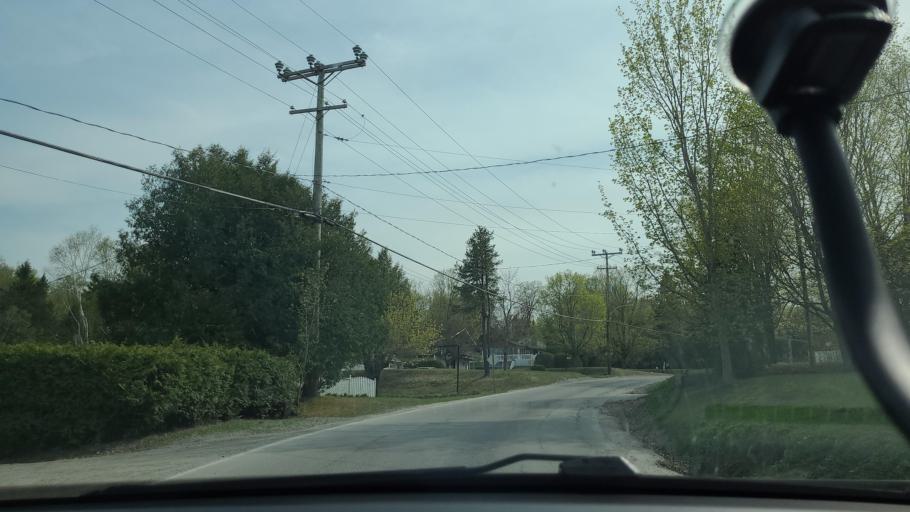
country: CA
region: Quebec
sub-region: Laurentides
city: Prevost
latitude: 45.8935
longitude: -74.0411
